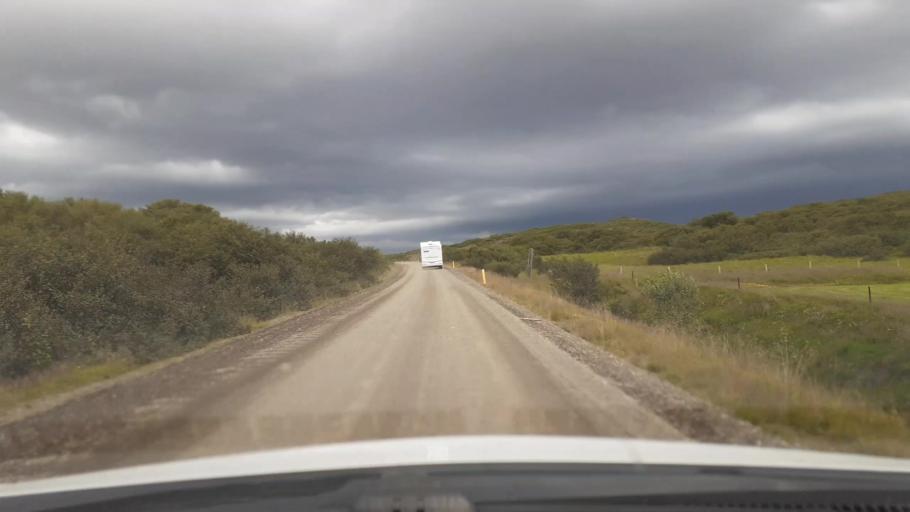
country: IS
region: West
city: Borgarnes
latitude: 64.5473
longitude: -21.6196
